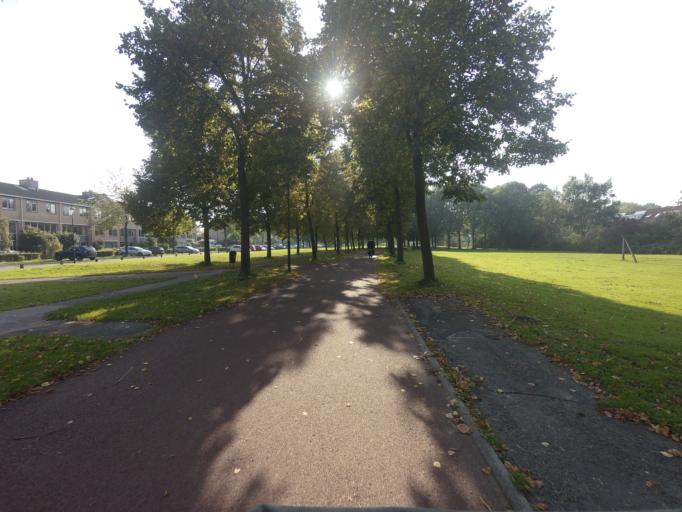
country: NL
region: Utrecht
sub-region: Gemeente Houten
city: Houten
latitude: 52.0381
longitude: 5.1798
